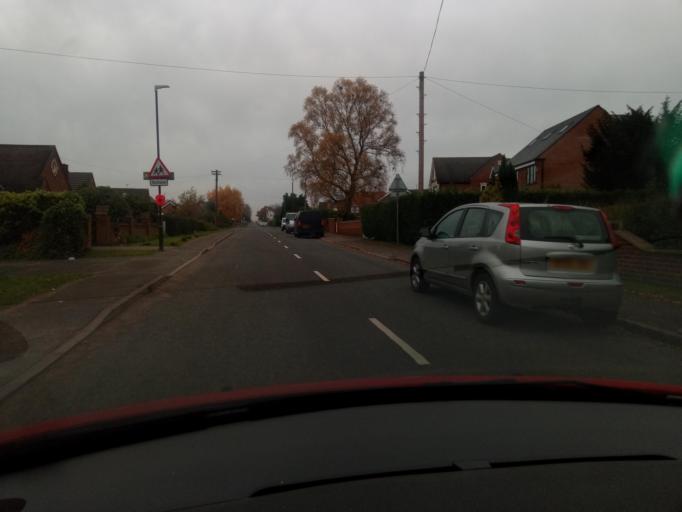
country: GB
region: England
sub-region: Derbyshire
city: Borrowash
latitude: 52.8638
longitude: -1.3850
